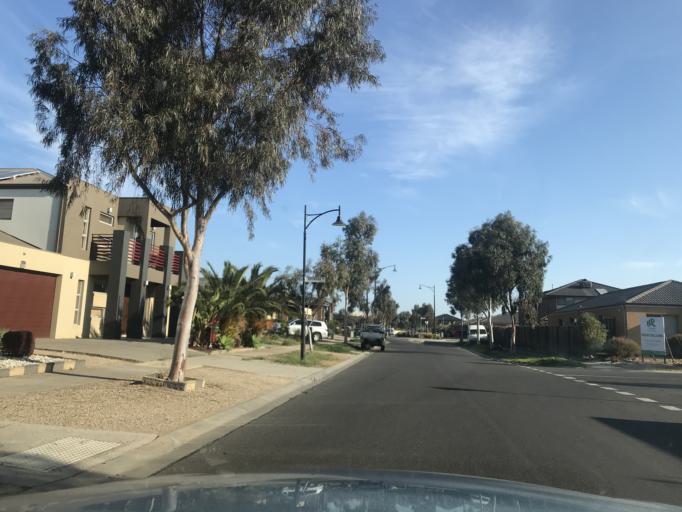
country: AU
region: Victoria
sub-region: Wyndham
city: Williams Landing
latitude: -37.8567
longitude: 144.7248
